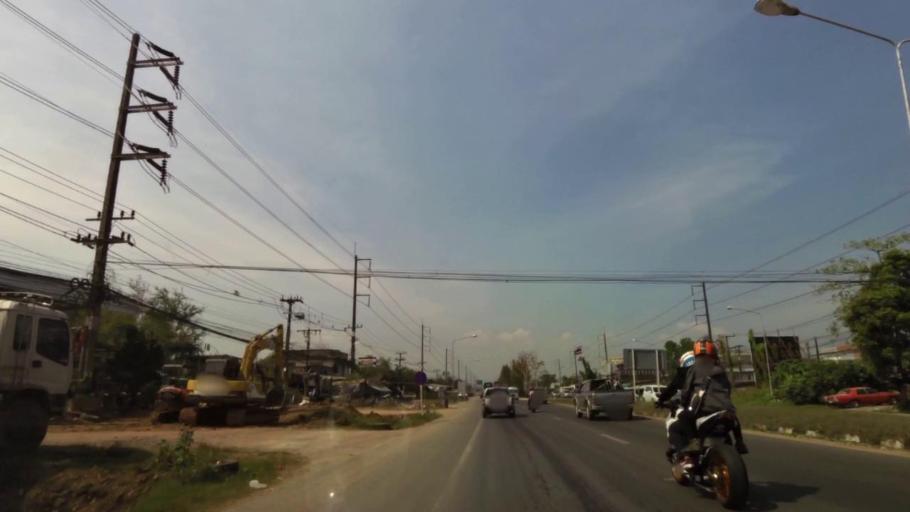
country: TH
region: Chanthaburi
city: Chanthaburi
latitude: 12.6248
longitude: 102.1509
